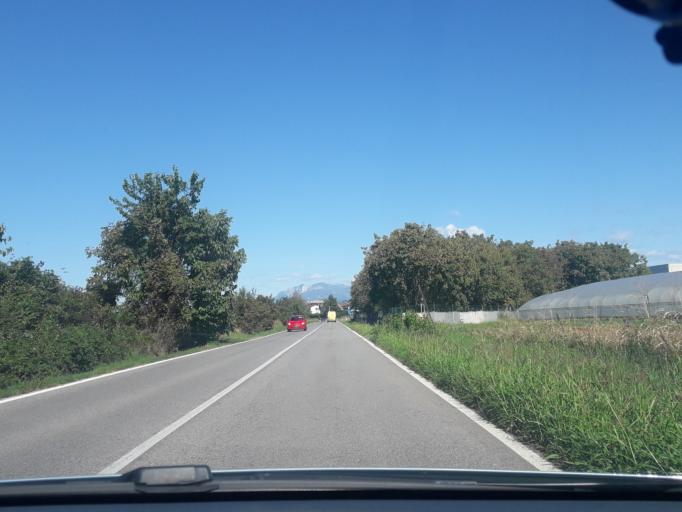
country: IT
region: Friuli Venezia Giulia
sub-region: Provincia di Udine
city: Basaldella
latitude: 46.0318
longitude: 13.2362
